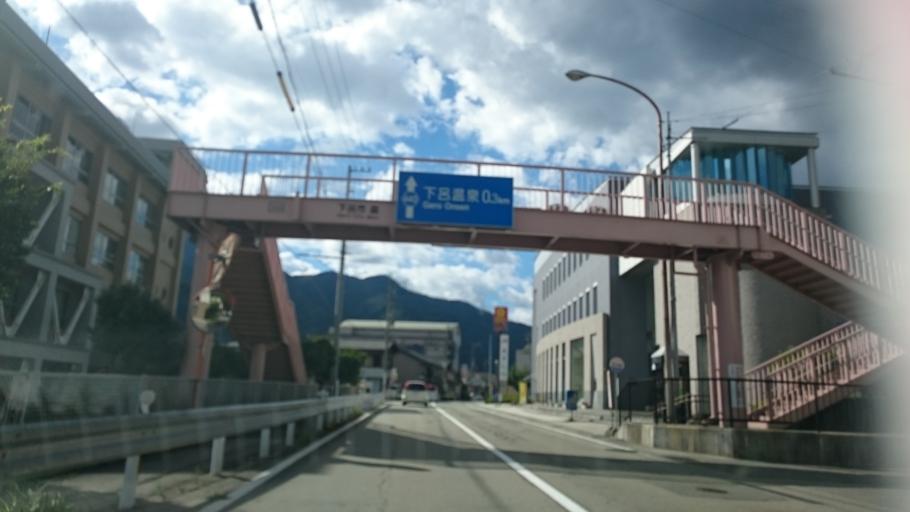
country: JP
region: Gifu
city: Gujo
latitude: 35.8014
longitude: 137.2482
